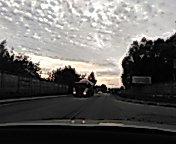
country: RU
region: Moskovskaya
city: Skhodnya
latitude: 55.9418
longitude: 37.2686
